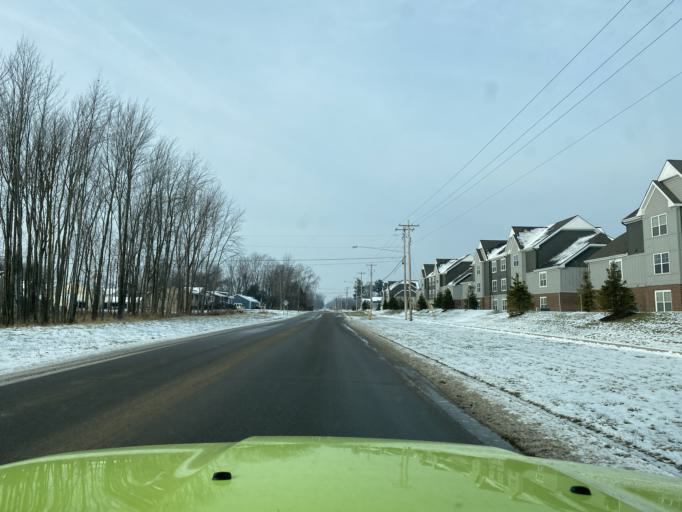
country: US
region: Michigan
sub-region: Ottawa County
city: Allendale
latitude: 42.9578
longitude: -85.9143
